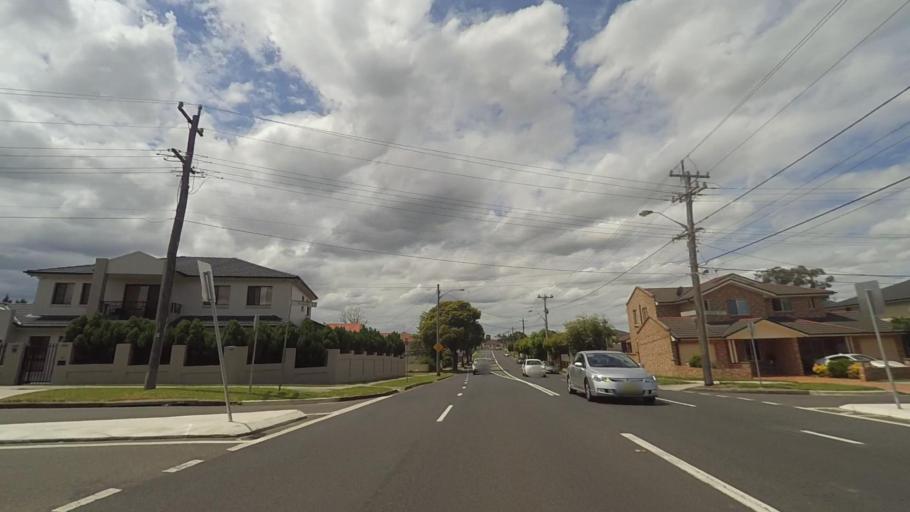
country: AU
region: New South Wales
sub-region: Fairfield
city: Fairfield Heights
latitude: -33.8658
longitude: 150.9498
